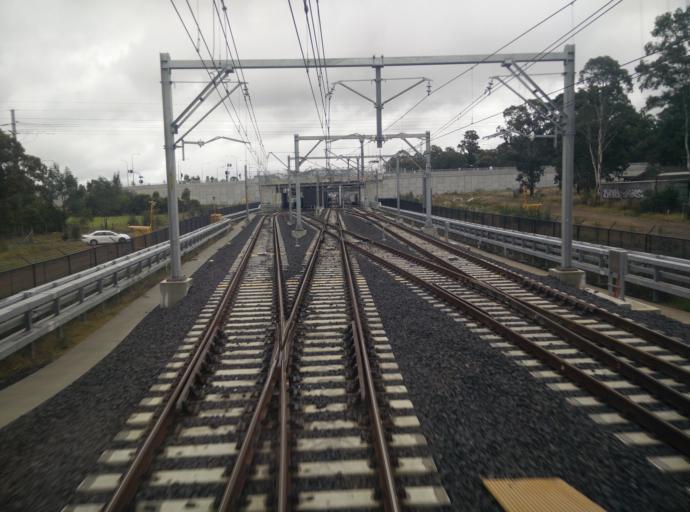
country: AU
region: New South Wales
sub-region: Blacktown
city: Rouse Hill
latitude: -33.6907
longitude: 150.9088
